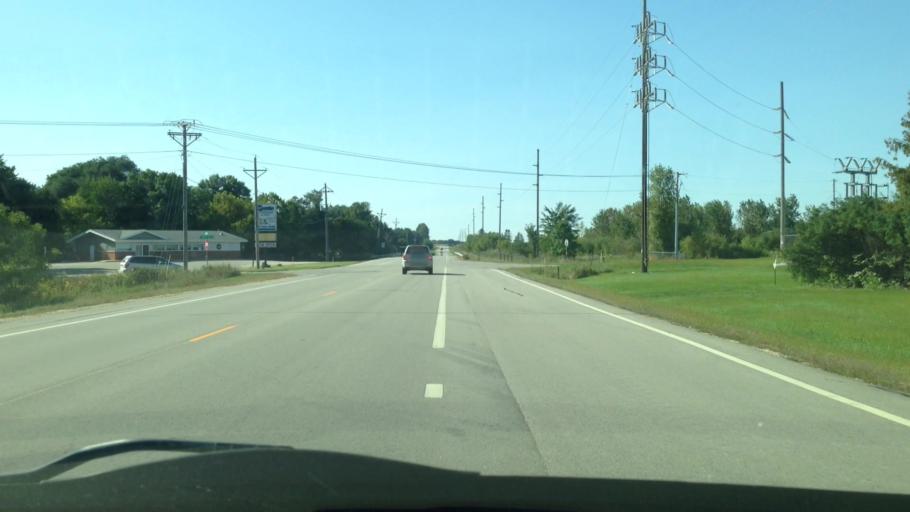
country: US
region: Minnesota
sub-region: Olmsted County
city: Eyota
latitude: 43.9908
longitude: -92.2281
